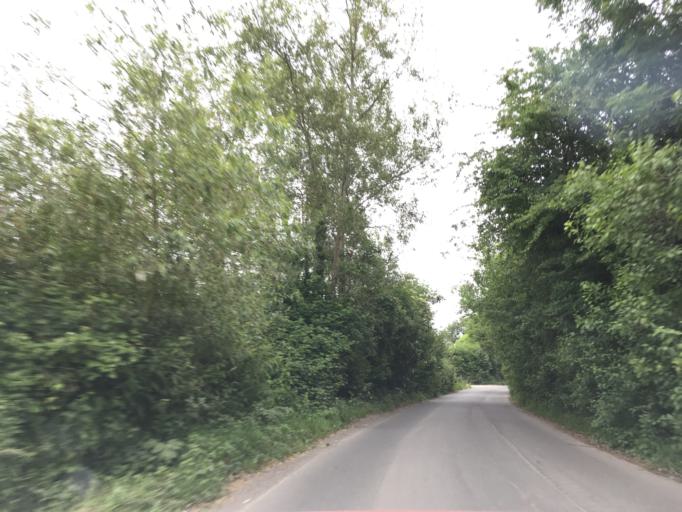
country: GB
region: England
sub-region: Gloucestershire
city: Stonehouse
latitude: 51.7808
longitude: -2.3604
